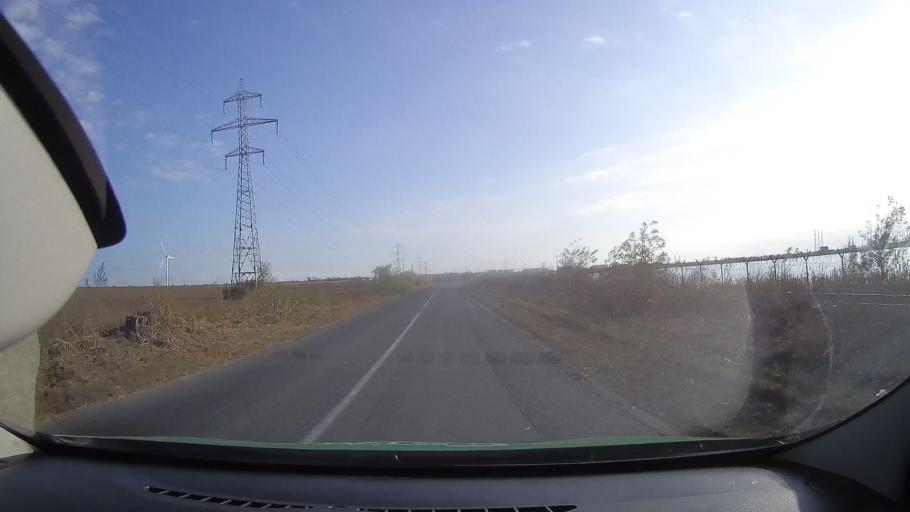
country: RO
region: Constanta
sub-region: Comuna Corbu
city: Corbu
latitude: 44.3655
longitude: 28.6724
